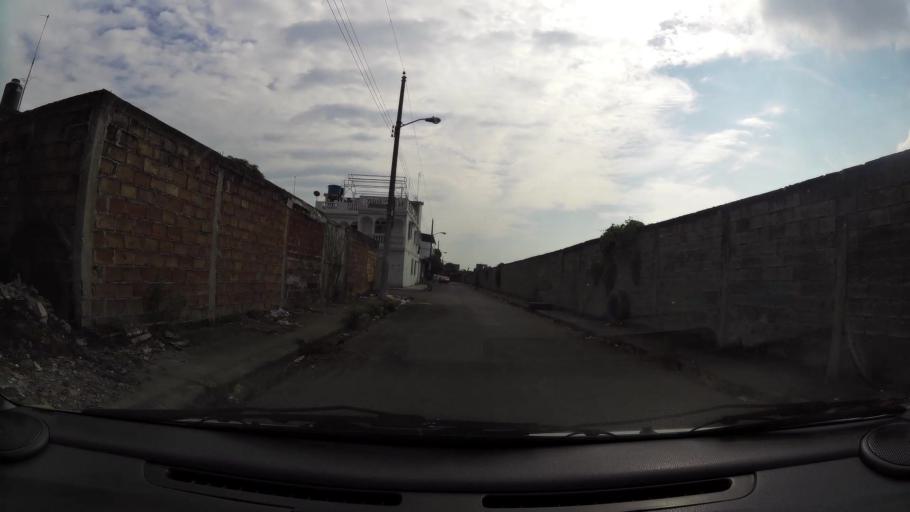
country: EC
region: Guayas
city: Guayaquil
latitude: -2.2599
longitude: -79.8996
